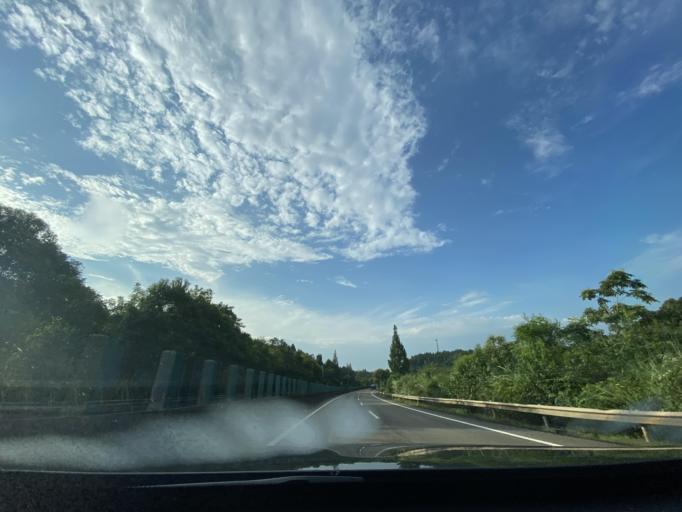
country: CN
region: Sichuan
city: Jiancheng
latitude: 30.3060
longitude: 104.5782
